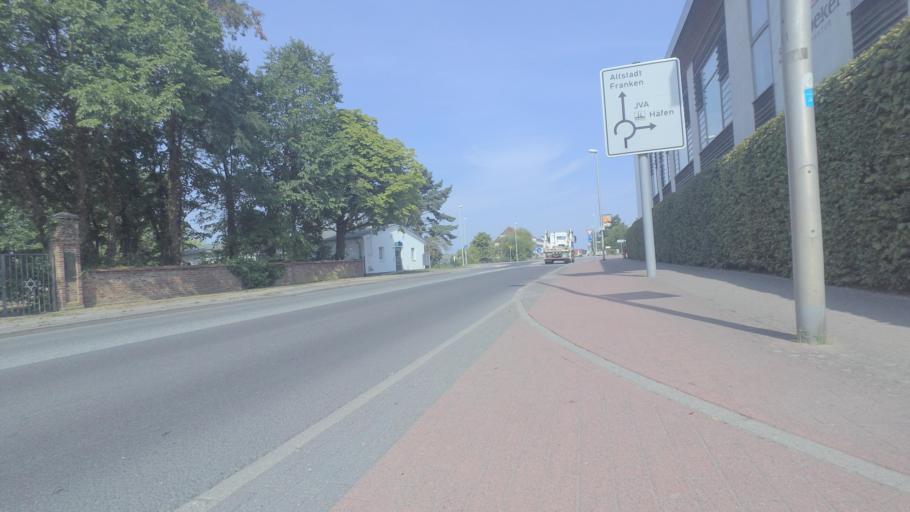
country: DE
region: Mecklenburg-Vorpommern
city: Stralsund
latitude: 54.2910
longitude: 13.0941
